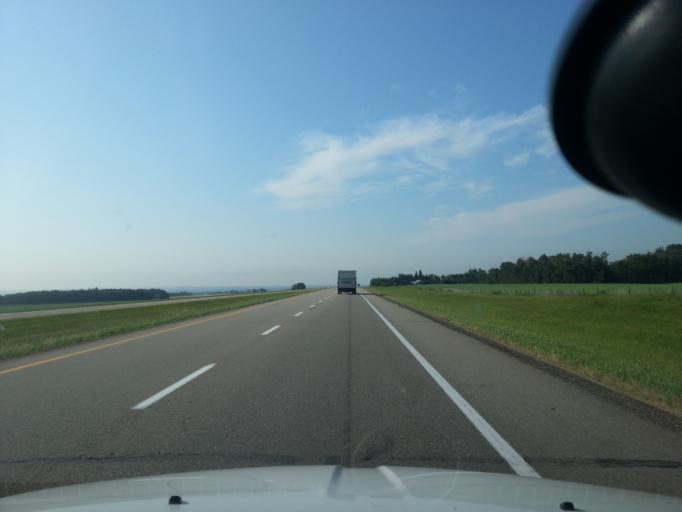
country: CA
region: Alberta
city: Ponoka
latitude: 52.7043
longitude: -113.6441
